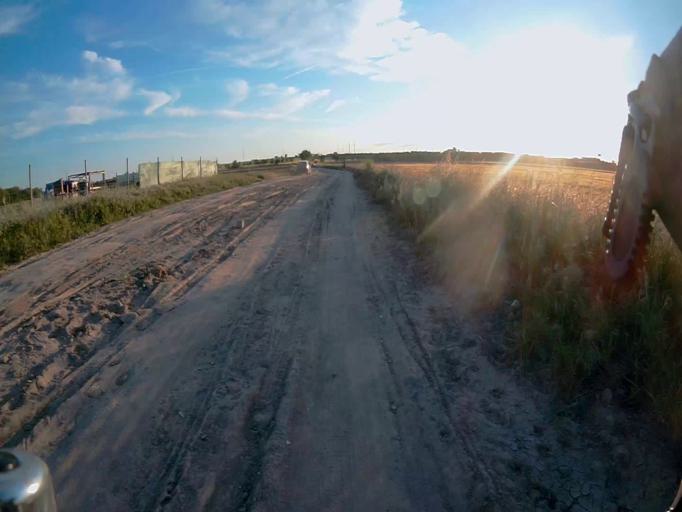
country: ES
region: Madrid
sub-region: Provincia de Madrid
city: Alcorcon
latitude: 40.3326
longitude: -3.8030
